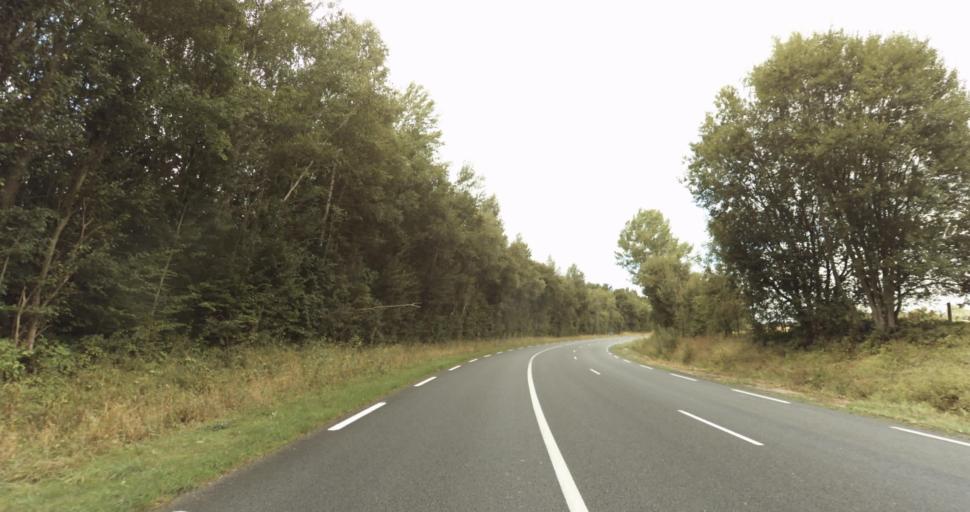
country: FR
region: Lower Normandy
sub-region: Departement de l'Orne
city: Gace
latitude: 48.8466
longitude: 0.2619
